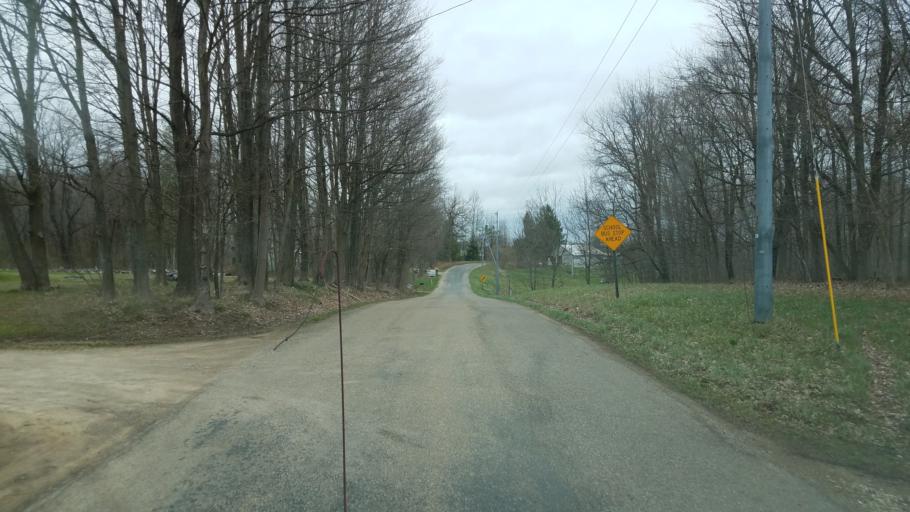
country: US
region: Ohio
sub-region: Knox County
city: Mount Vernon
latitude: 40.4662
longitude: -82.4299
